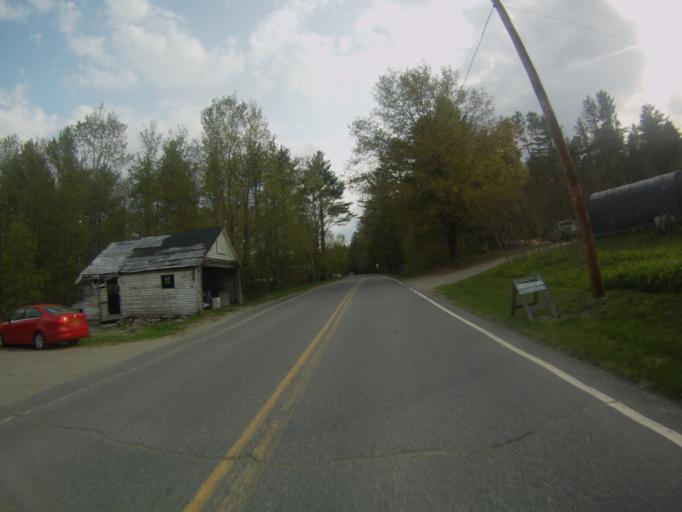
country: US
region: New York
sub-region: Warren County
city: Warrensburg
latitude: 43.8413
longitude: -73.8729
